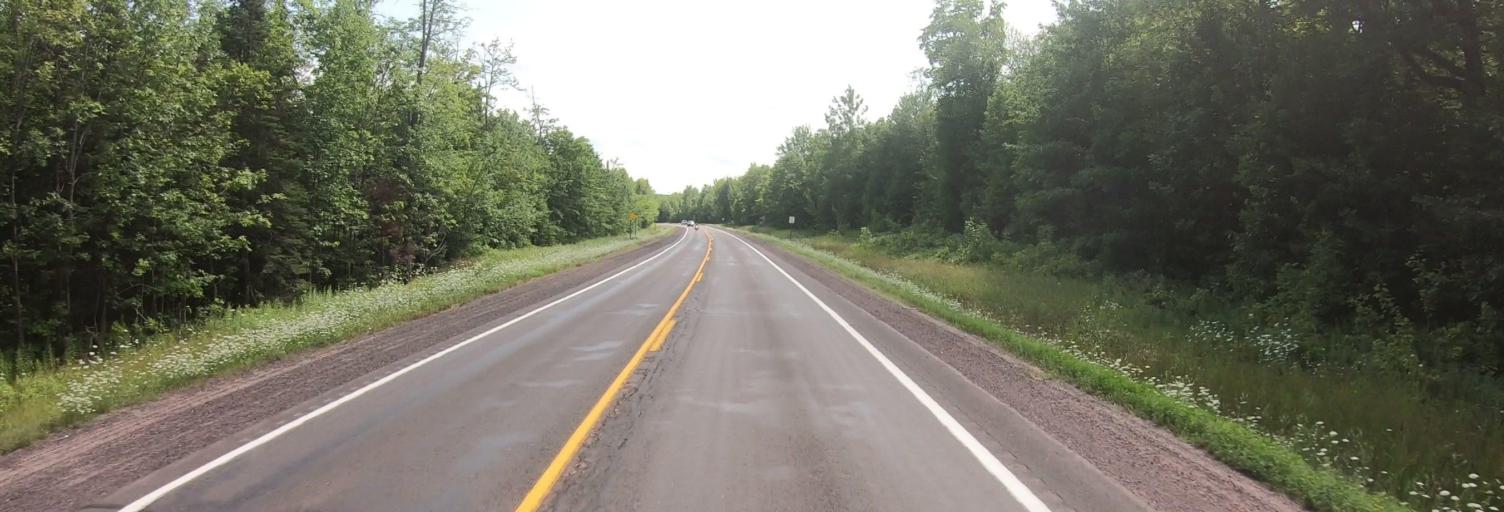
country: US
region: Michigan
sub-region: Ontonagon County
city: Ontonagon
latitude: 46.8307
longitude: -88.9961
